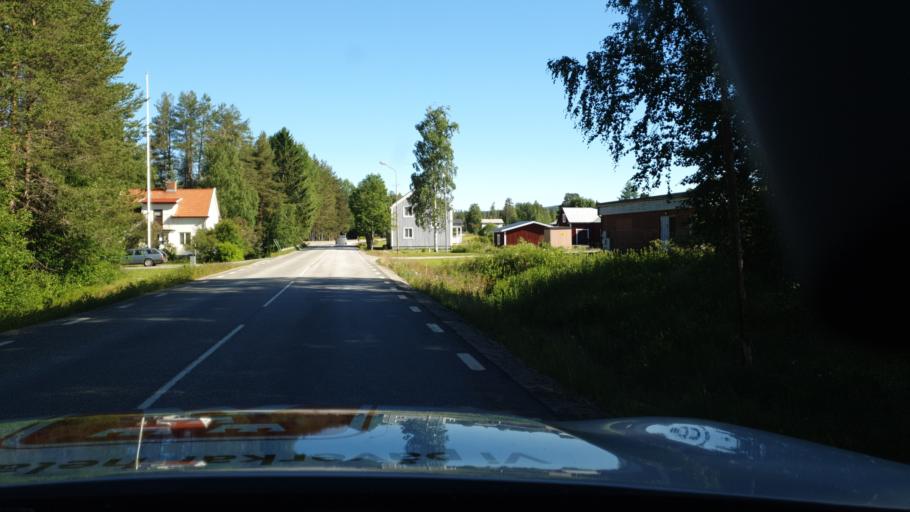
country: SE
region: Vaesterbotten
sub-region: Vindelns Kommun
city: Vindeln
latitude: 64.2237
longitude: 19.7071
